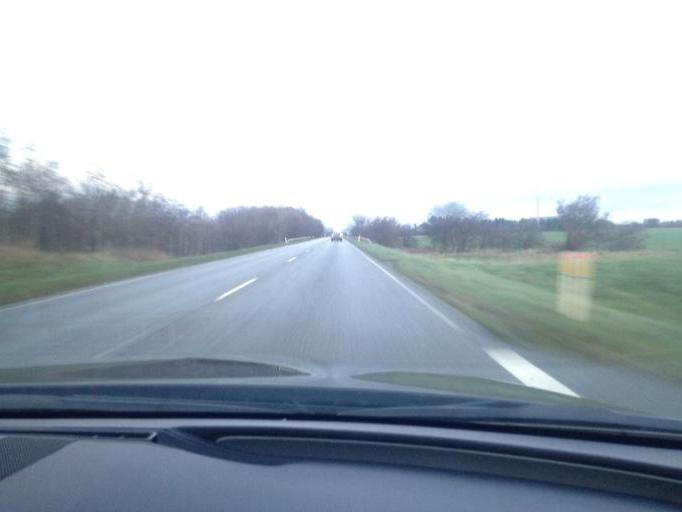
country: DK
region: South Denmark
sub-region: Kolding Kommune
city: Kolding
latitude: 55.5593
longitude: 9.4894
